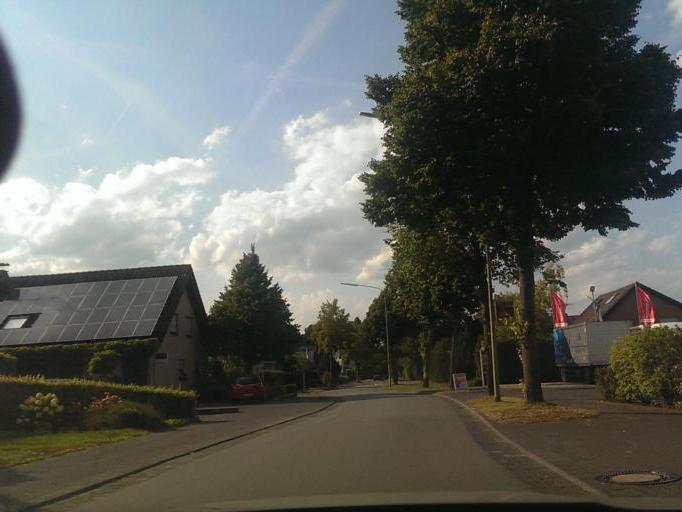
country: DE
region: North Rhine-Westphalia
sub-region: Regierungsbezirk Detmold
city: Delbruck
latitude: 51.7418
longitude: 8.5131
